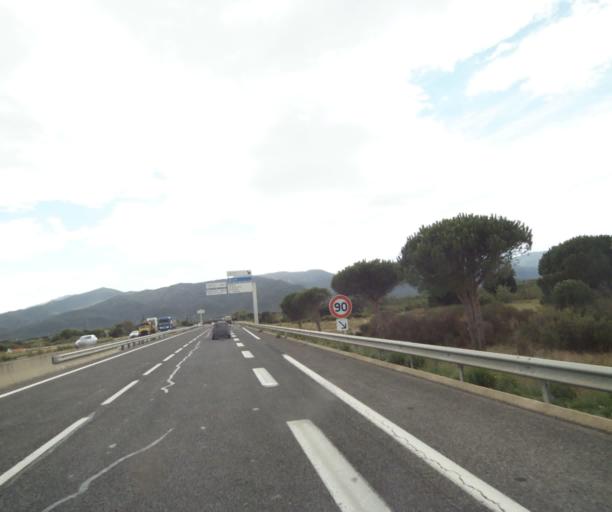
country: FR
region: Languedoc-Roussillon
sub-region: Departement des Pyrenees-Orientales
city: Argelers
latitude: 42.5546
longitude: 3.0060
